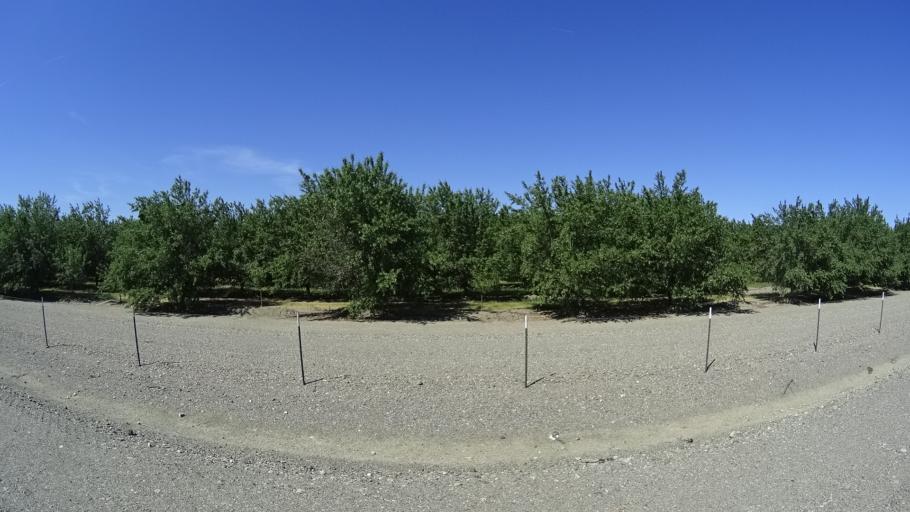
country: US
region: California
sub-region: Glenn County
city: Orland
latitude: 39.7294
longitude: -122.1410
